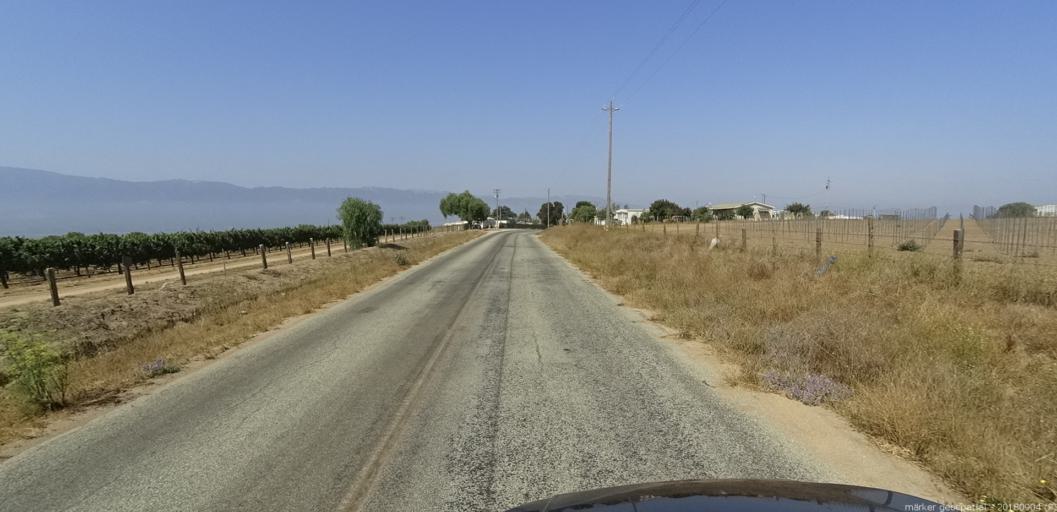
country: US
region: California
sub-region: Monterey County
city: Gonzales
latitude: 36.5039
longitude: -121.3805
